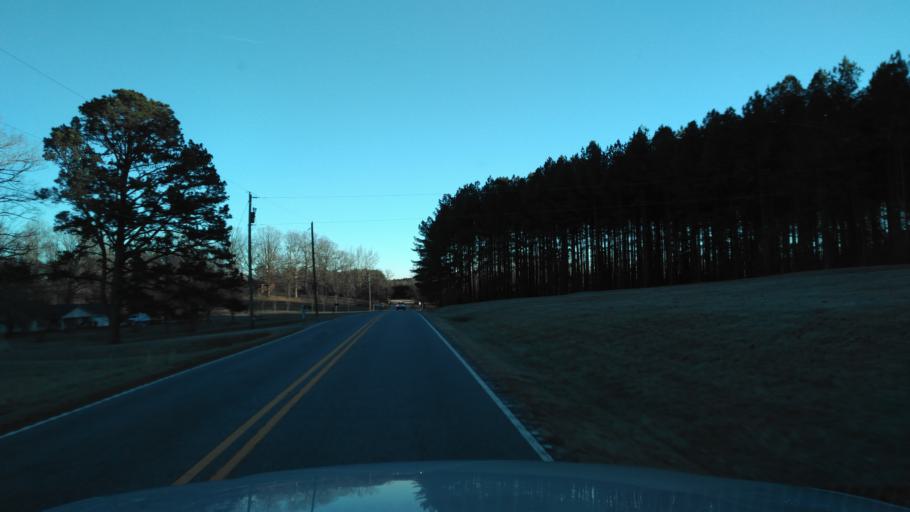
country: US
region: South Carolina
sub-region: Spartanburg County
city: Landrum
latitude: 35.2031
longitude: -82.0531
